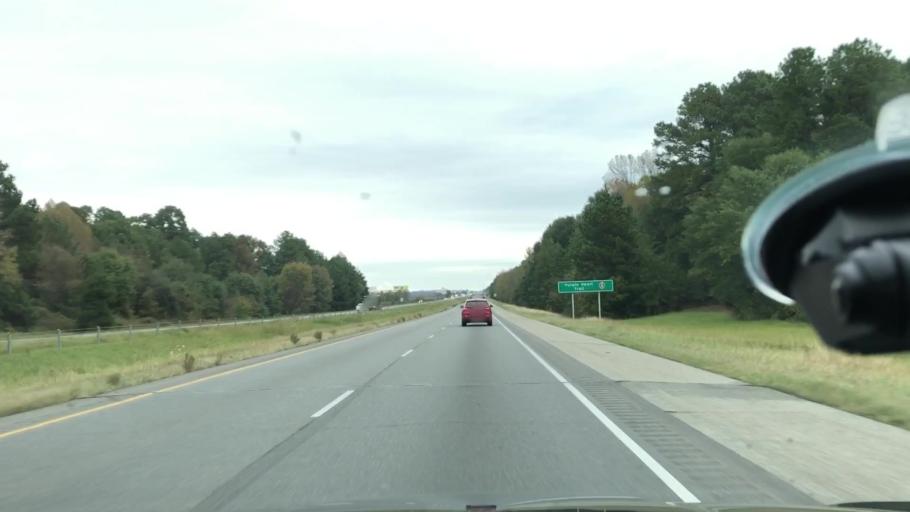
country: US
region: Arkansas
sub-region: Miller County
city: Texarkana
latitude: 33.4886
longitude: -93.9723
